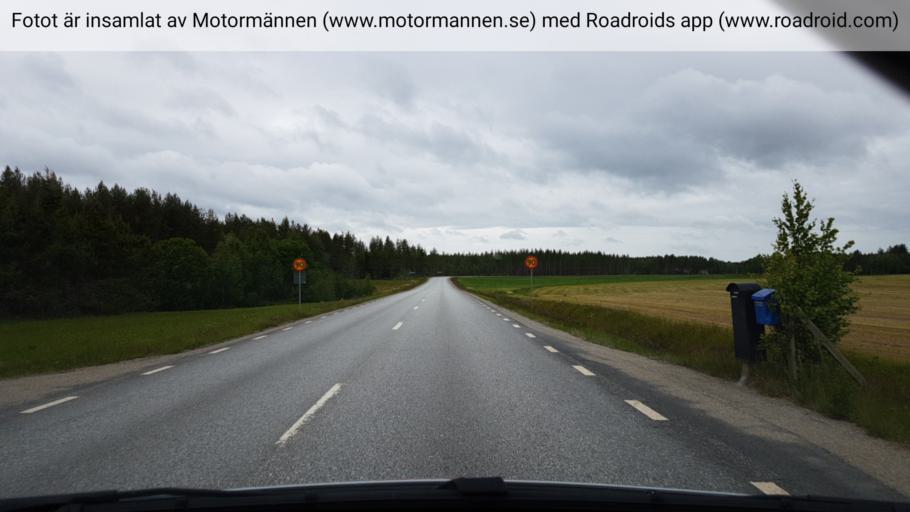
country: SE
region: Vaesterbotten
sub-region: Vindelns Kommun
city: Vindeln
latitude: 64.1133
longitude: 19.5776
